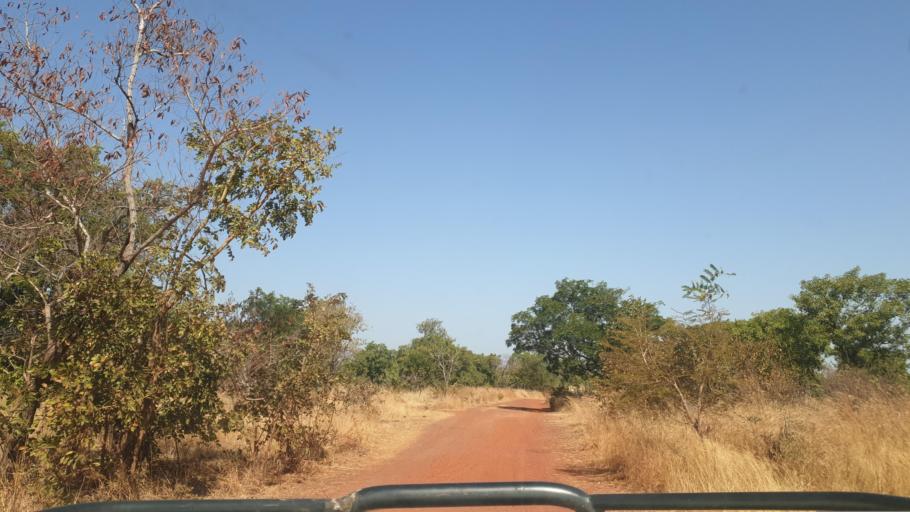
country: ML
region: Koulikoro
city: Dioila
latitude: 11.9132
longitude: -6.9848
